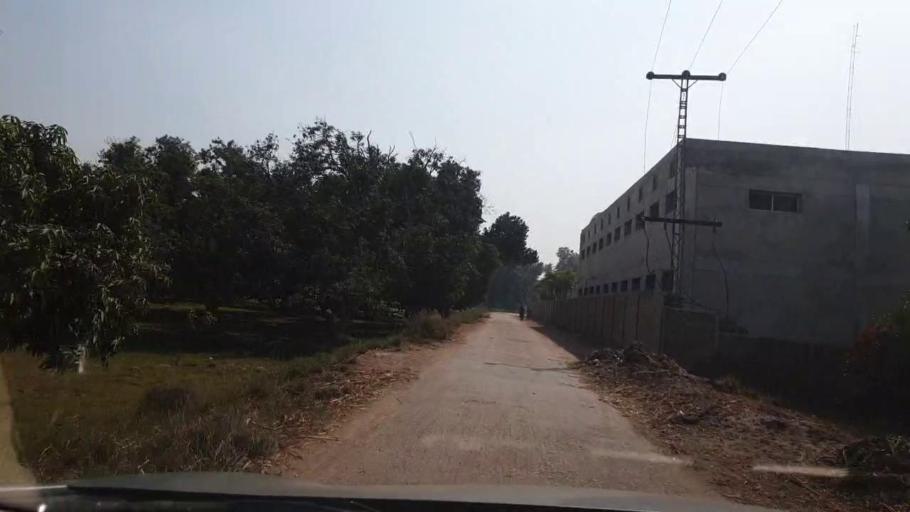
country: PK
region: Sindh
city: Tando Allahyar
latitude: 25.4845
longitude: 68.7708
